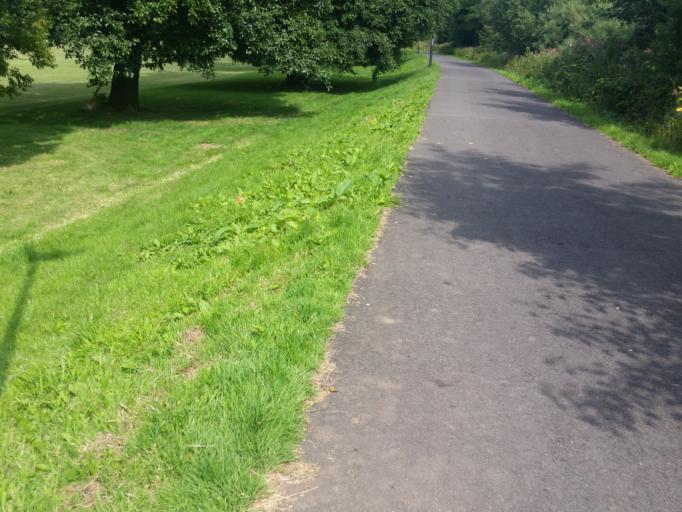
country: GB
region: England
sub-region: Derby
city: Derby
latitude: 52.9066
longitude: -1.4360
